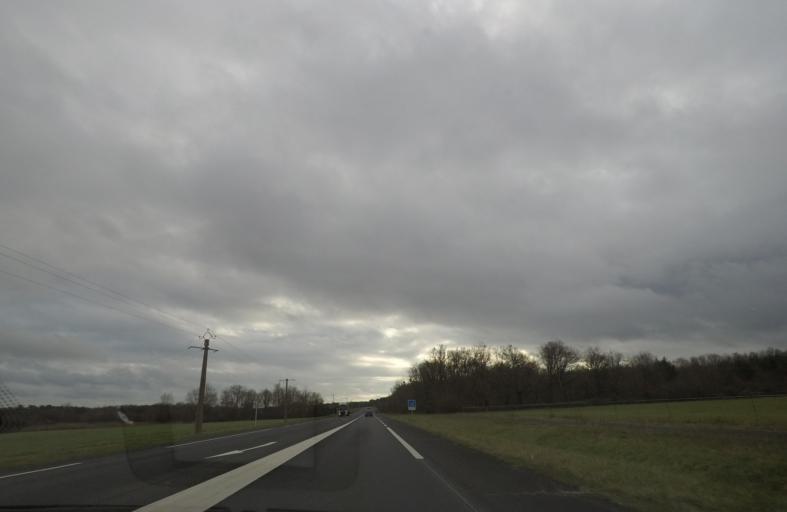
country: FR
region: Centre
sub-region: Departement du Loir-et-Cher
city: Soings-en-Sologne
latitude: 47.4463
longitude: 1.5398
